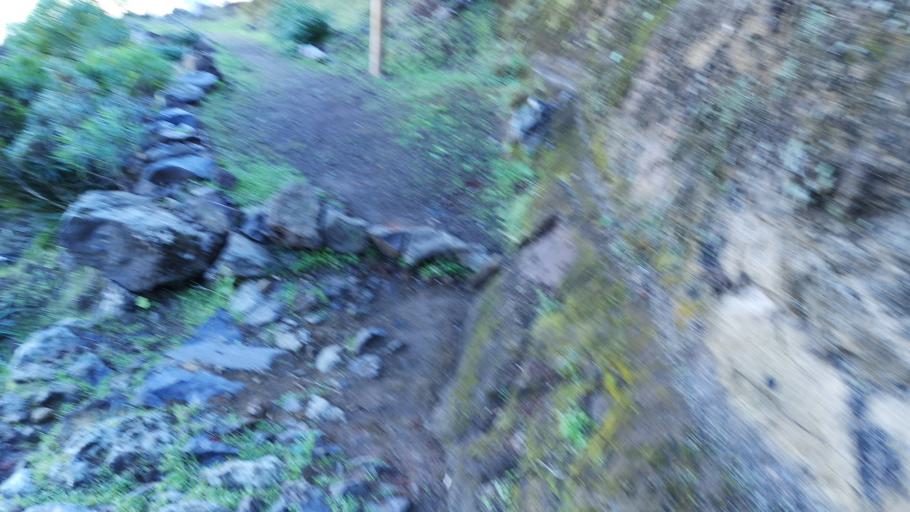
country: ES
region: Canary Islands
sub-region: Provincia de Santa Cruz de Tenerife
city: Alajero
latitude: 28.0808
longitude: -17.2262
